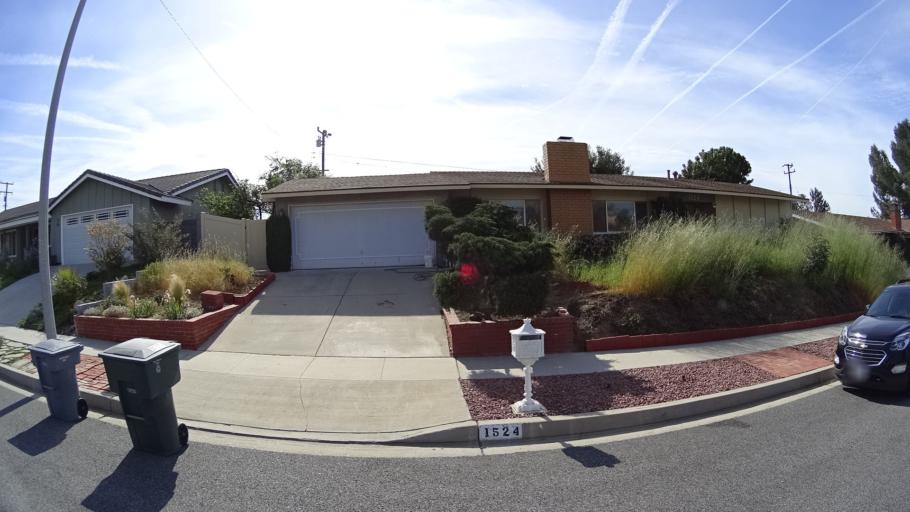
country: US
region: California
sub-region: Ventura County
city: Thousand Oaks
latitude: 34.1994
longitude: -118.8766
